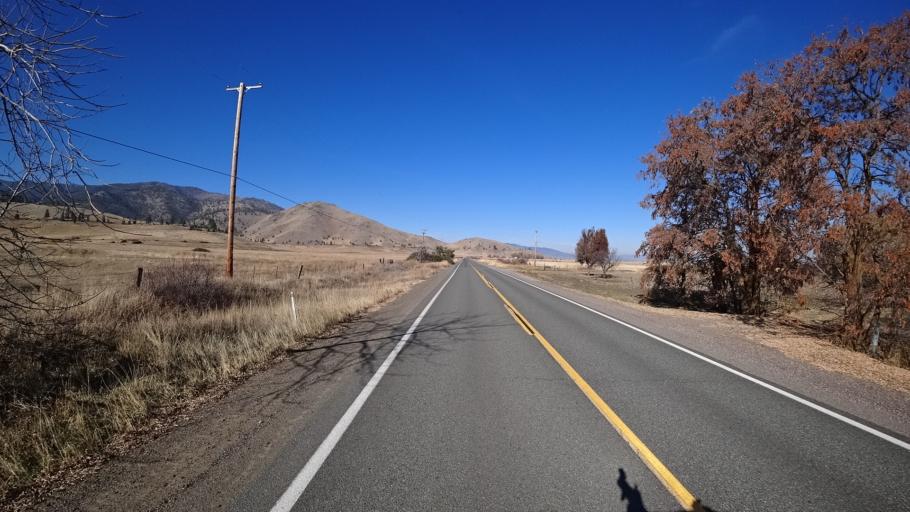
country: US
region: California
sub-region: Siskiyou County
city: Weed
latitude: 41.4494
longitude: -122.4525
